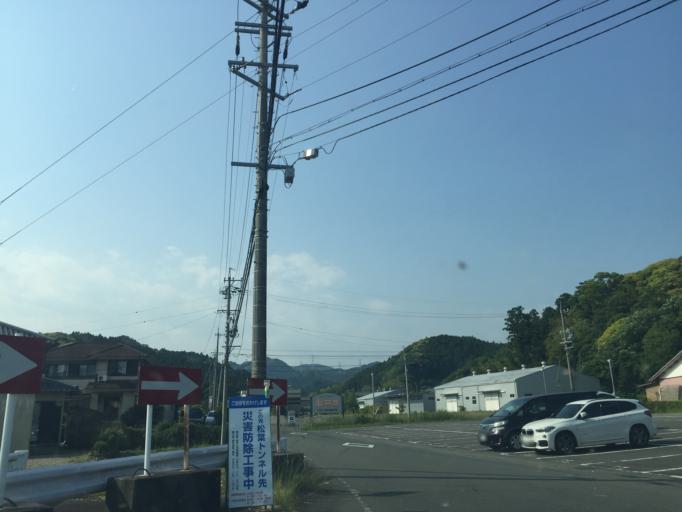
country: JP
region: Shizuoka
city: Kakegawa
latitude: 34.8175
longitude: 138.0346
